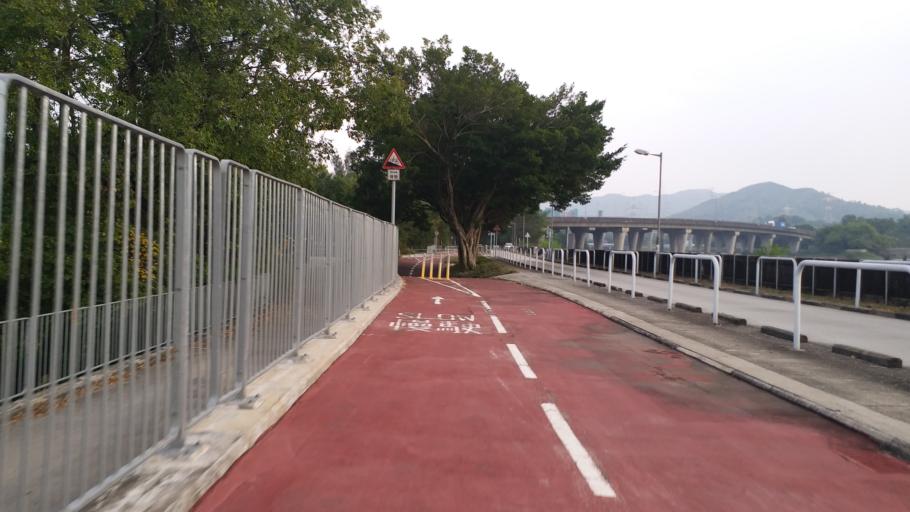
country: HK
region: Yuen Long
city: Yuen Long Kau Hui
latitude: 22.4557
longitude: 114.0485
